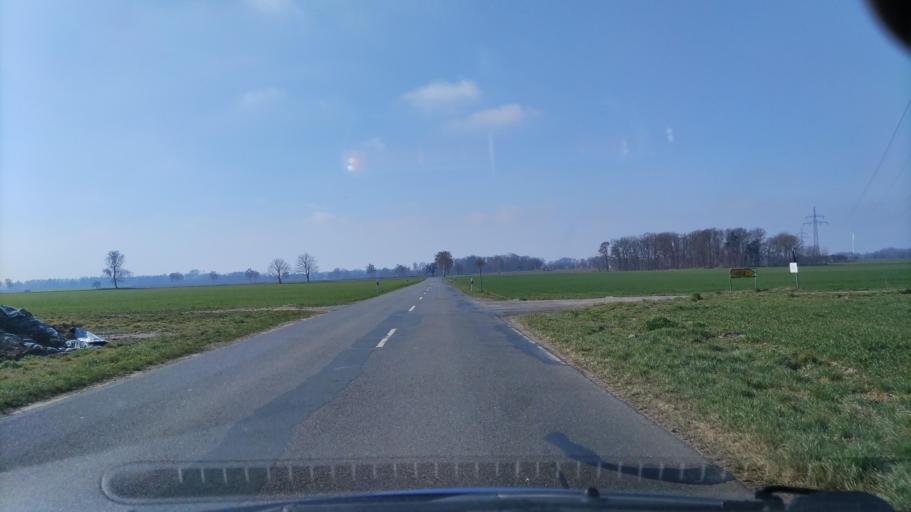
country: DE
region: Lower Saxony
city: Kusten
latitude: 52.9501
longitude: 11.0579
